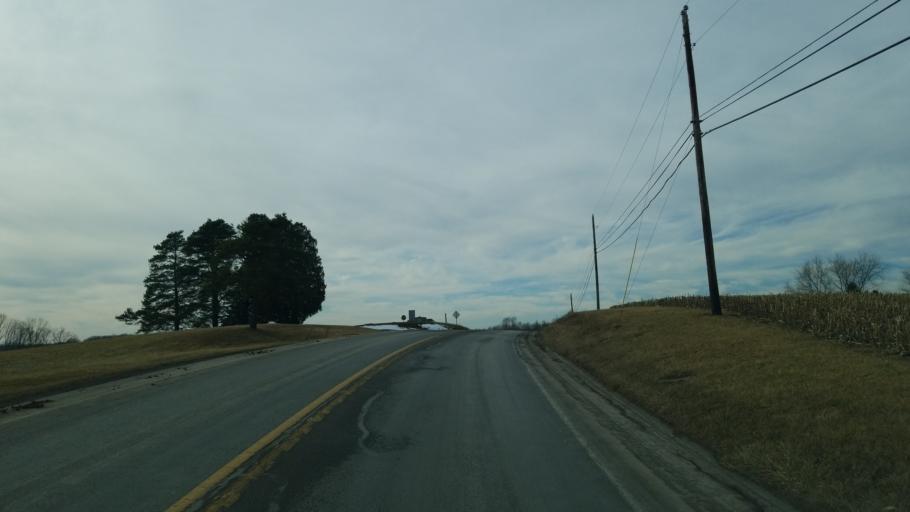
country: US
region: Pennsylvania
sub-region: Jefferson County
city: Punxsutawney
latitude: 40.8850
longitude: -79.0467
